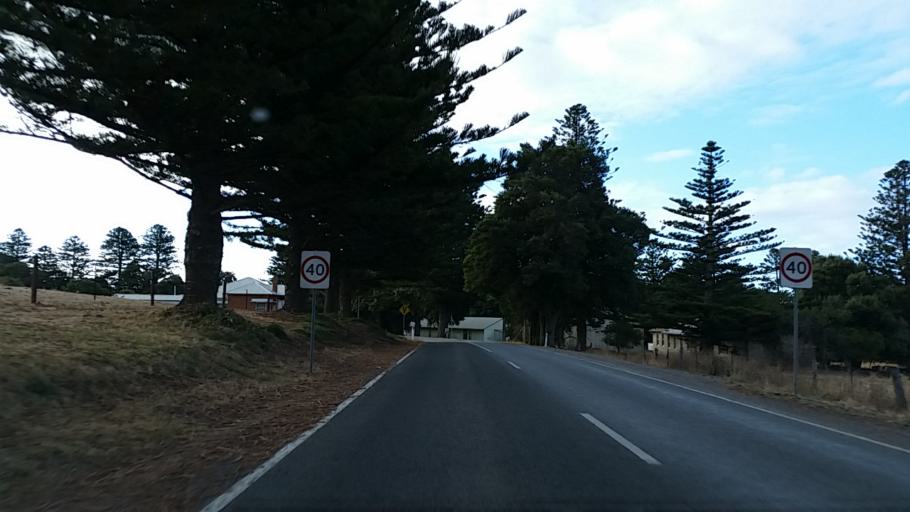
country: AU
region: South Australia
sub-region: Yankalilla
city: Normanville
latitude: -35.5280
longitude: 138.1908
